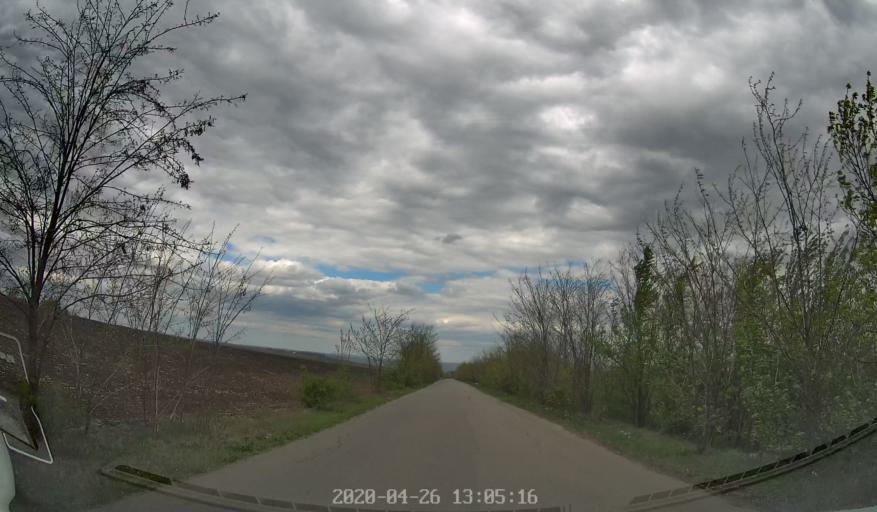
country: MD
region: Chisinau
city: Vadul lui Voda
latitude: 47.0746
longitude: 29.0660
